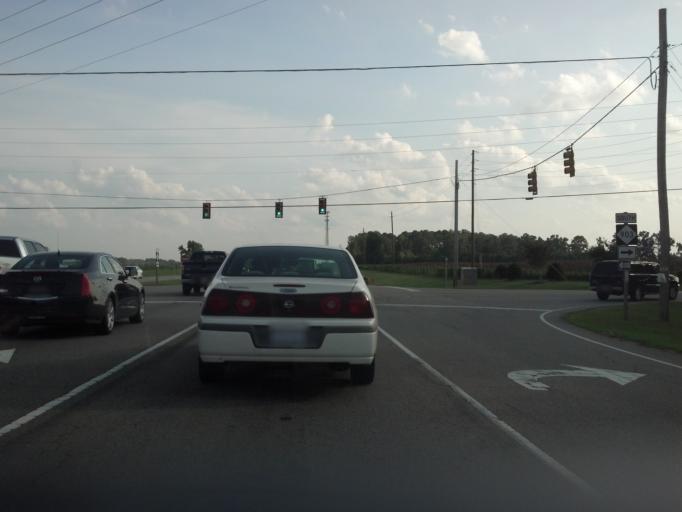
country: US
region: North Carolina
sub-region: Pitt County
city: Winterville
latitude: 35.5284
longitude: -77.4082
